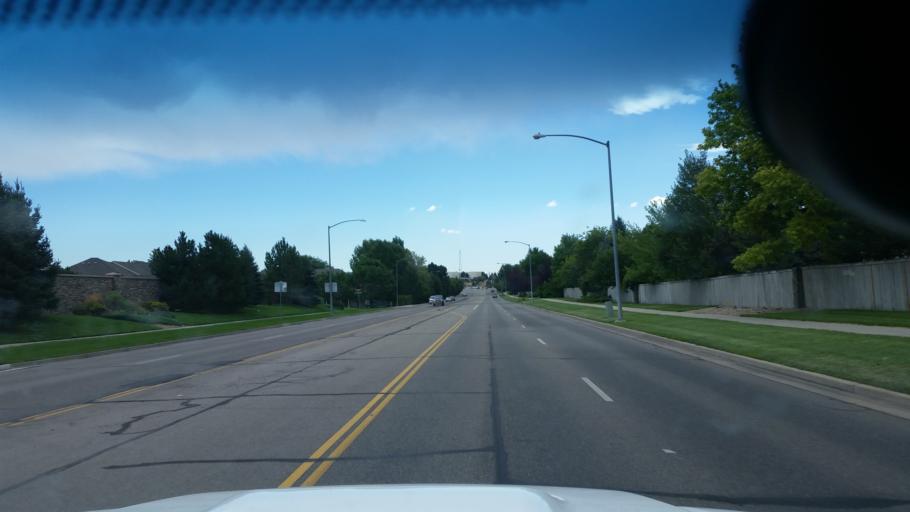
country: US
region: Colorado
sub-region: Adams County
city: Northglenn
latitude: 39.8996
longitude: -105.0050
